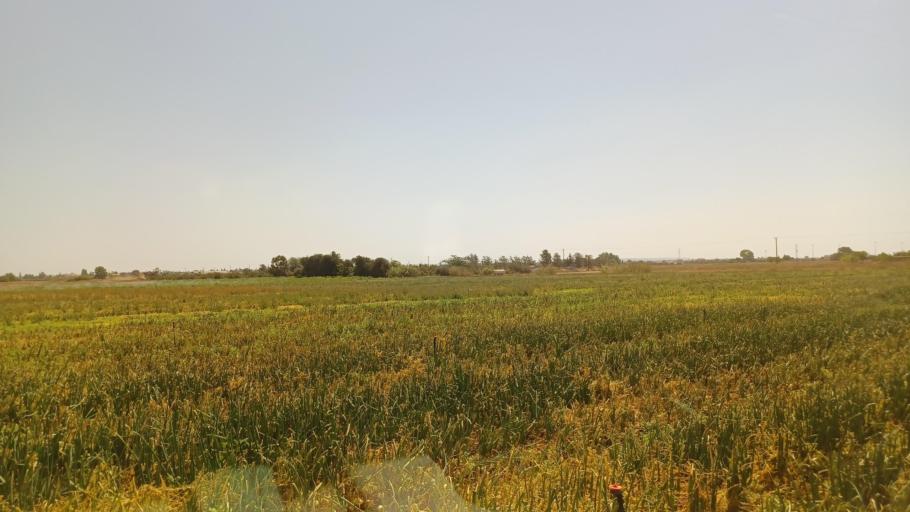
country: CY
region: Ammochostos
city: Avgorou
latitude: 35.0241
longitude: 33.8179
